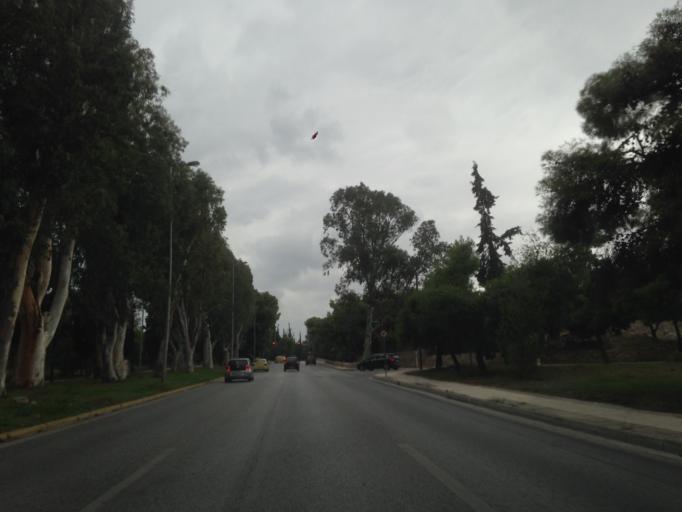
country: GR
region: Attica
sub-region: Nomarchia Anatolikis Attikis
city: Vouliagmeni
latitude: 37.8197
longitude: 23.7767
